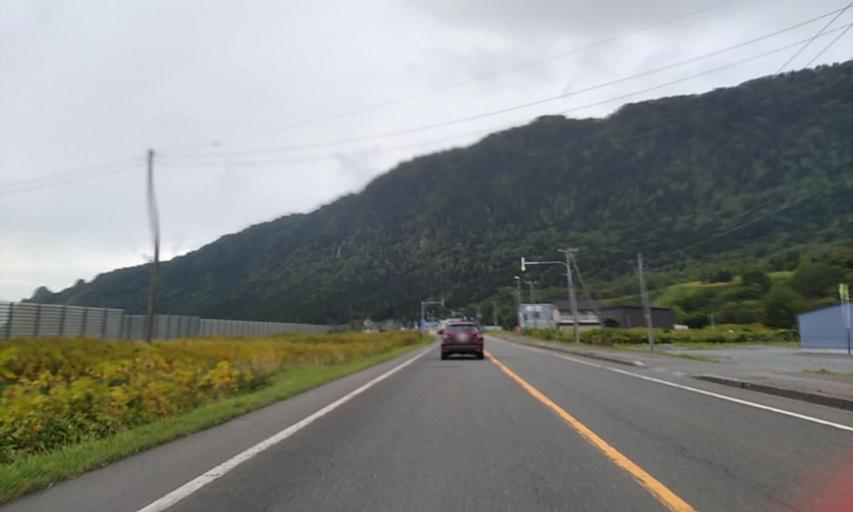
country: JP
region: Hokkaido
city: Nayoro
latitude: 45.0640
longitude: 142.4775
